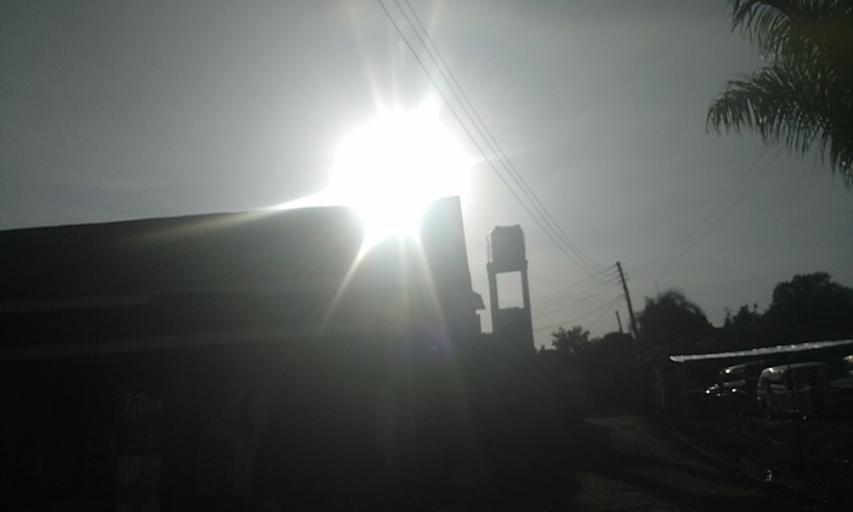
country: UG
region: Central Region
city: Kampala Central Division
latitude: 0.3660
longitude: 32.5979
